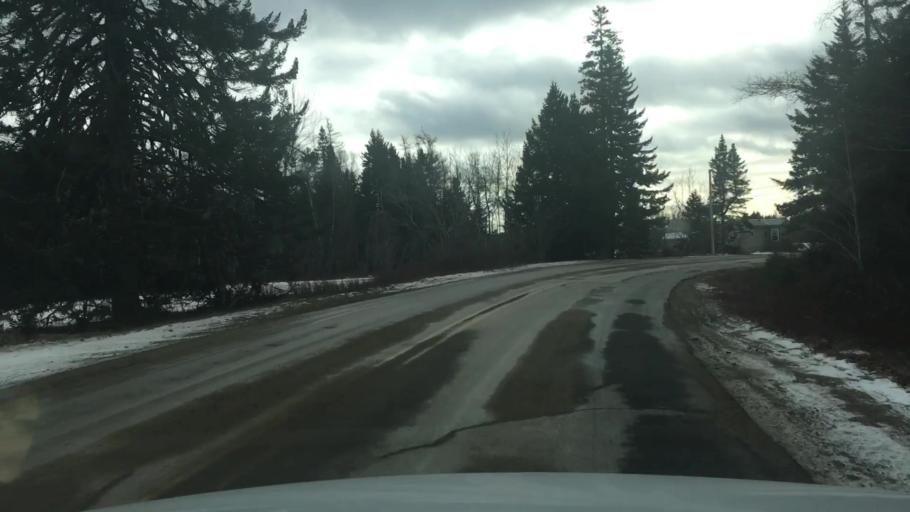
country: US
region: Maine
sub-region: Washington County
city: Machias
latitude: 44.6214
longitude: -67.4787
